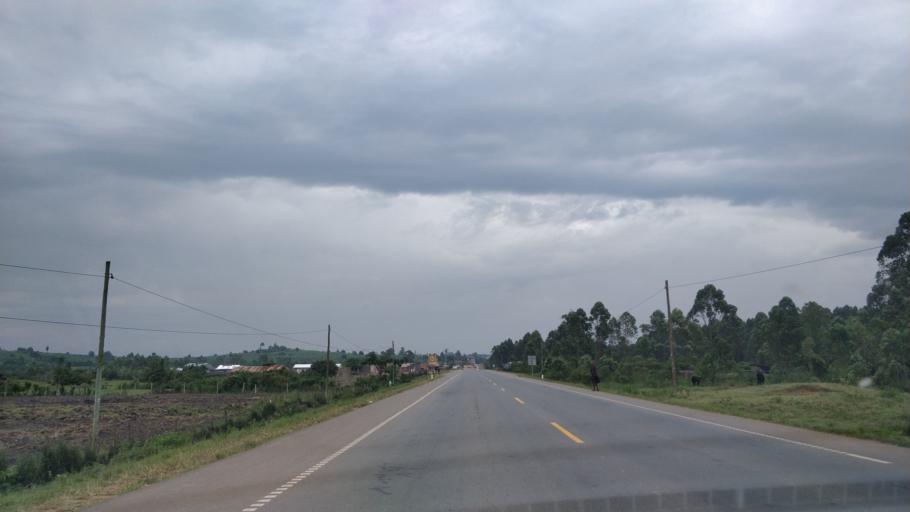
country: UG
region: Western Region
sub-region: Sheema District
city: Kibingo
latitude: -0.6649
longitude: 30.4491
